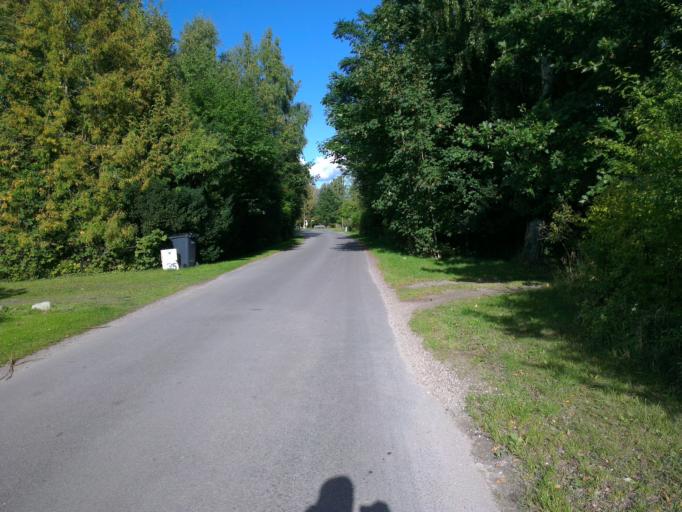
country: DK
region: Capital Region
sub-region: Frederikssund Kommune
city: Frederikssund
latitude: 55.7908
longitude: 12.0481
